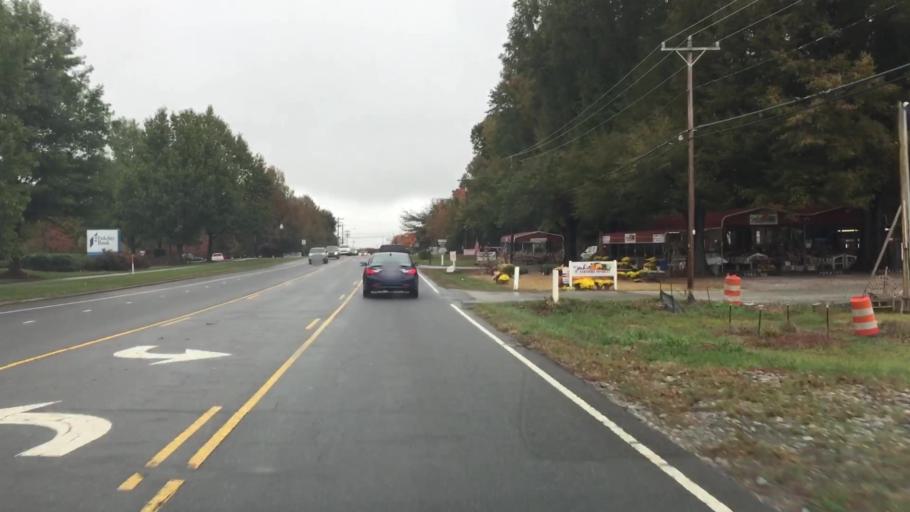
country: US
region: North Carolina
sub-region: Iredell County
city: Mooresville
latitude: 35.5905
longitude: -80.8730
